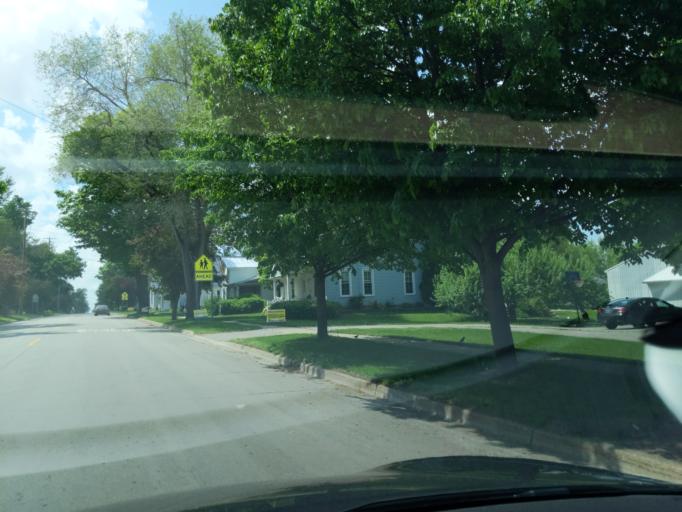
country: US
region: Michigan
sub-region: Ingham County
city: Williamston
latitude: 42.5559
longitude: -84.3036
